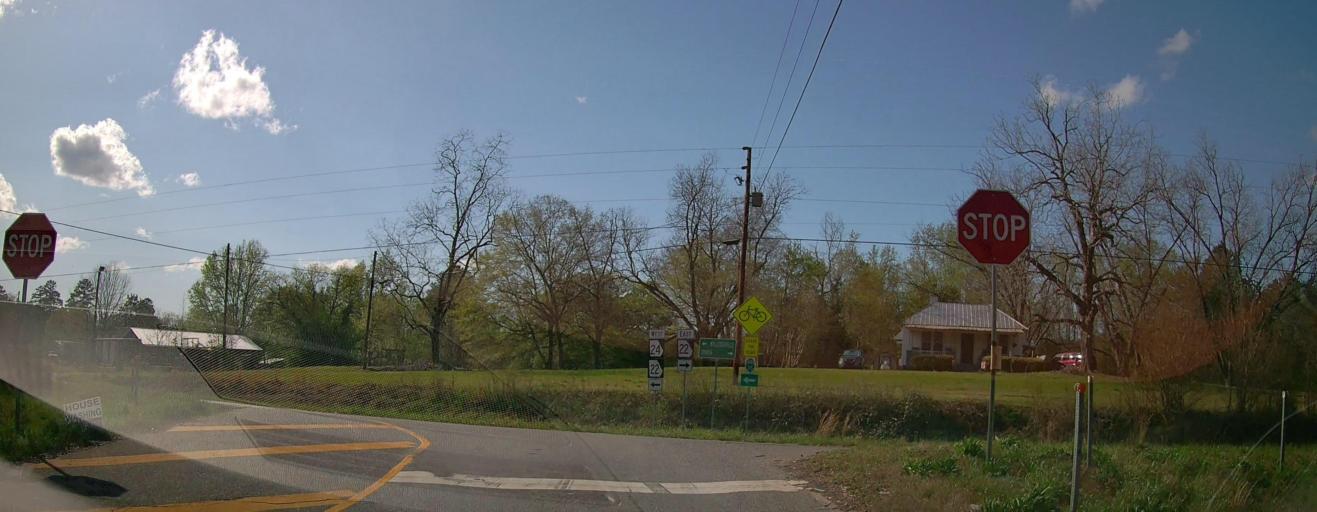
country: US
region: Georgia
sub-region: Baldwin County
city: Hardwick
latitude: 33.0807
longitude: -83.1612
